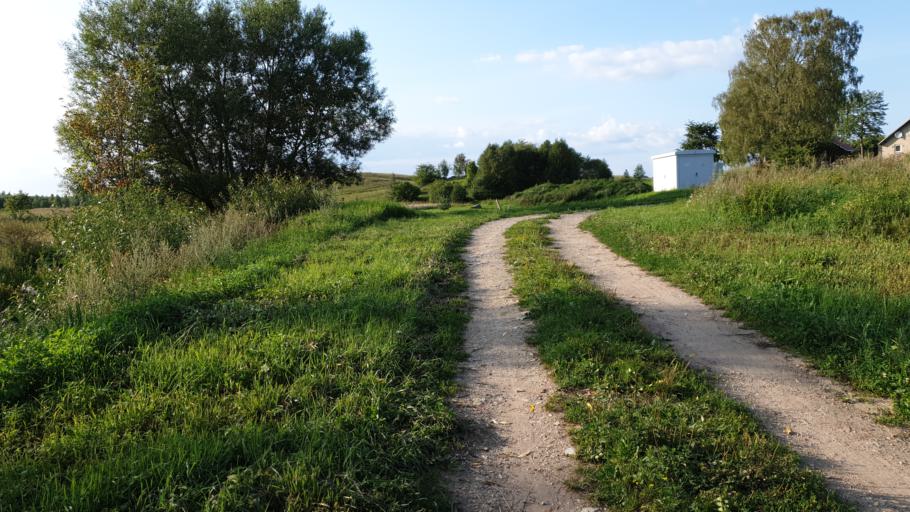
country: LT
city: Grigiskes
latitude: 54.7731
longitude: 25.0324
